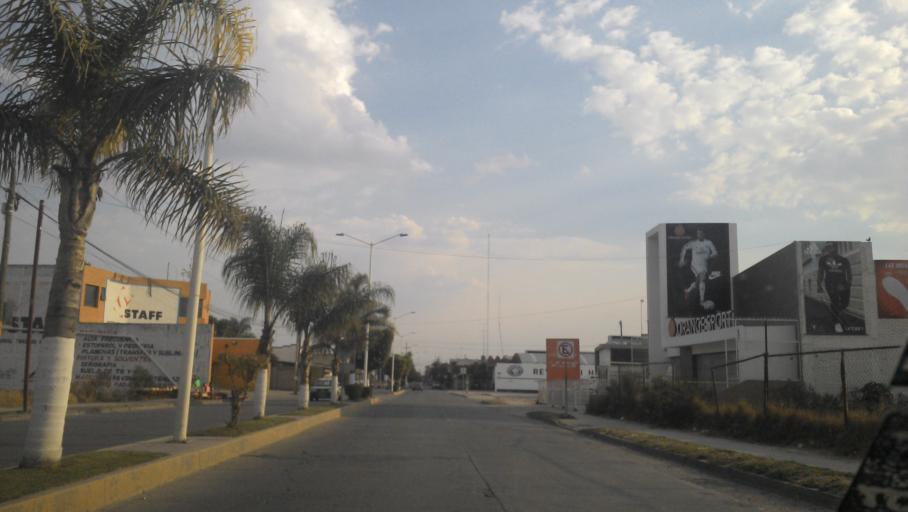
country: MX
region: Guanajuato
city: San Francisco del Rincon
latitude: 21.0277
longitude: -101.8526
